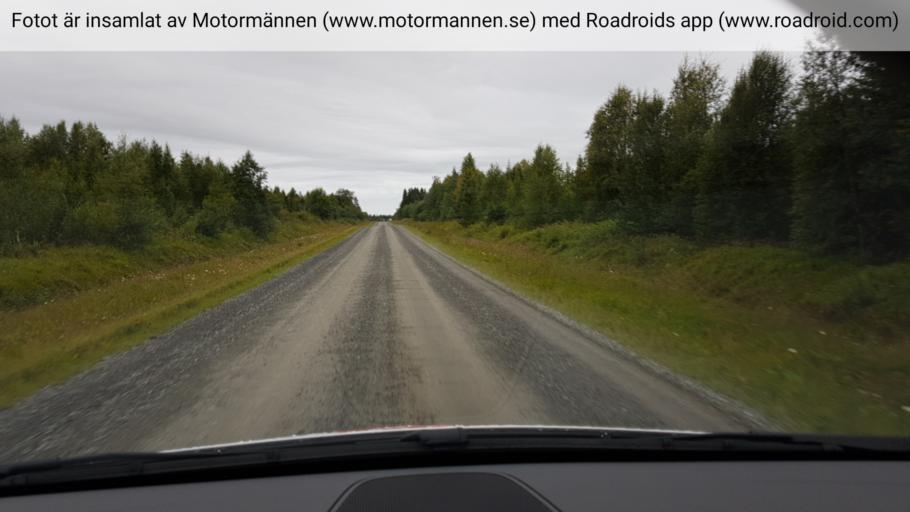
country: SE
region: Jaemtland
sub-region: OEstersunds Kommun
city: Lit
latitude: 63.6760
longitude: 14.8716
